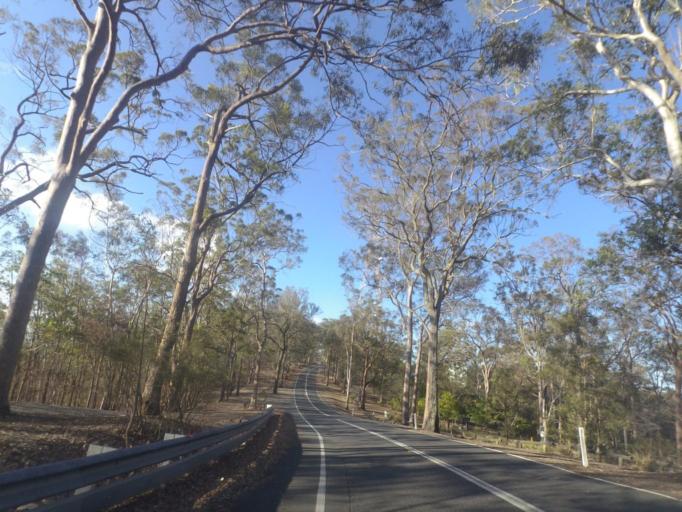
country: AU
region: Queensland
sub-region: Brisbane
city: Kenmore Hills
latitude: -27.4684
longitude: 152.9430
